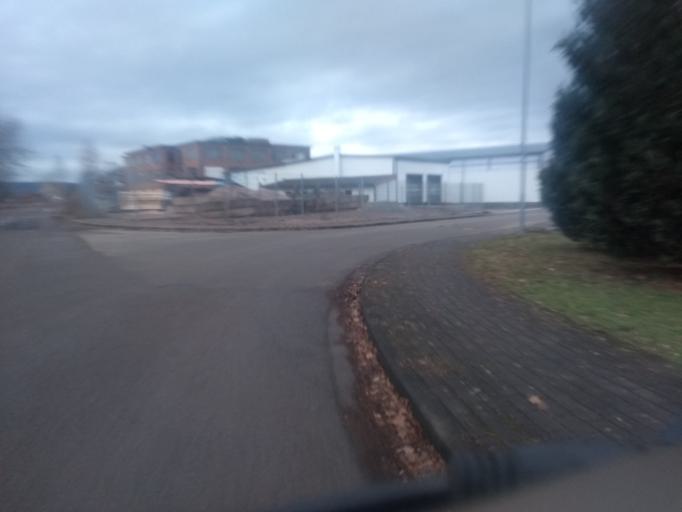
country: DE
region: Thuringia
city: Immelborn
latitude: 50.7892
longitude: 10.2844
